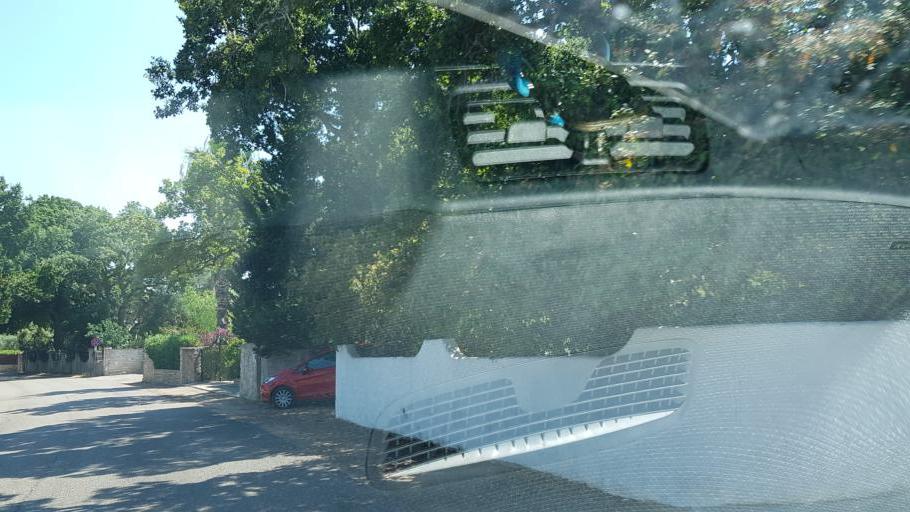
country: IT
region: Apulia
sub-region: Provincia di Lecce
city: Nardo
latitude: 40.1509
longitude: 17.9816
